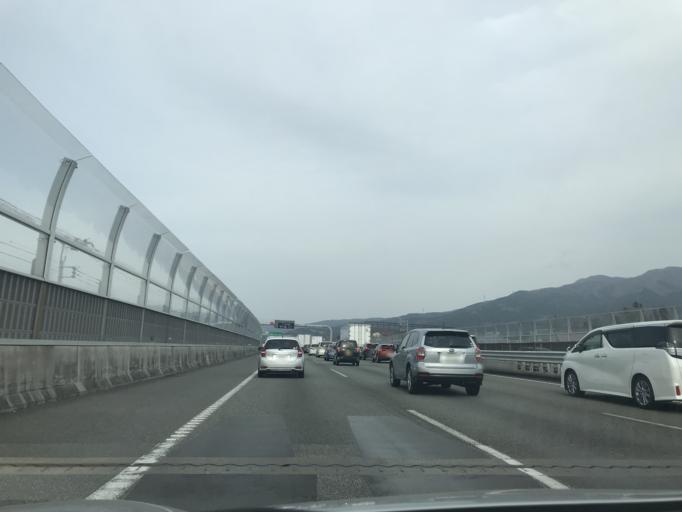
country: JP
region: Shizuoka
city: Gotemba
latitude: 35.2917
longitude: 138.9424
